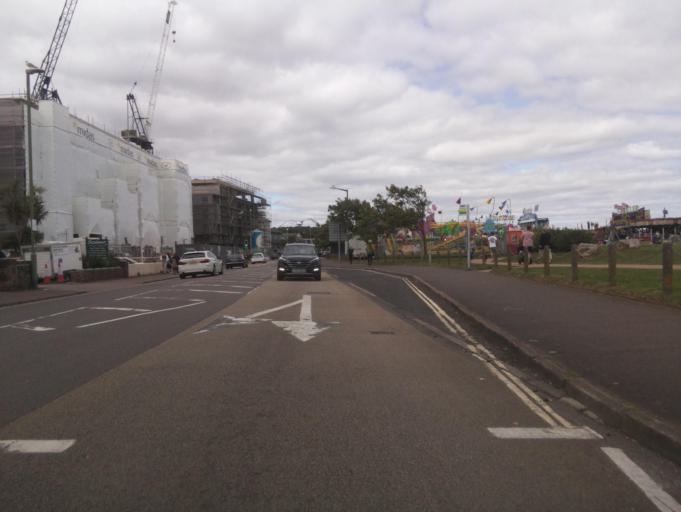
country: GB
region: England
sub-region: Borough of Torbay
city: Paignton
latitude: 50.4360
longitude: -3.5602
